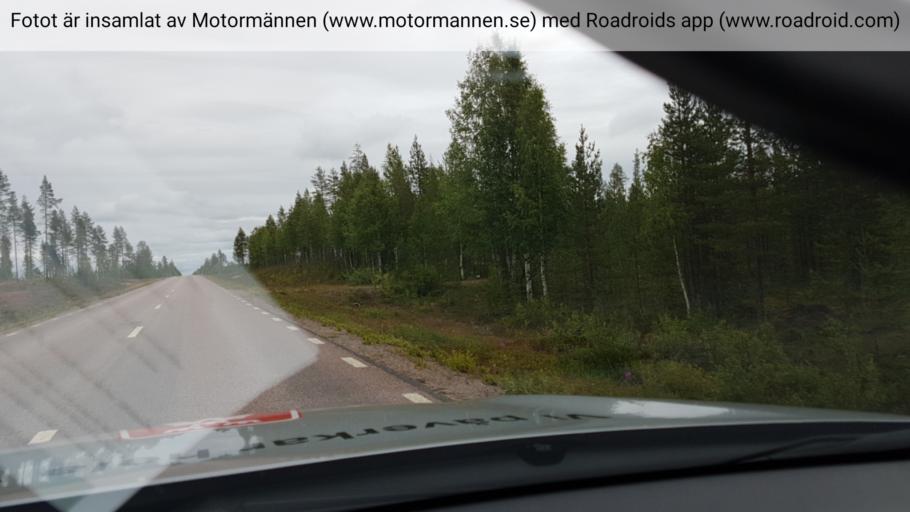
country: SE
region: Norrbotten
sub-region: Overkalix Kommun
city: OEverkalix
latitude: 67.0849
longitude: 22.5505
